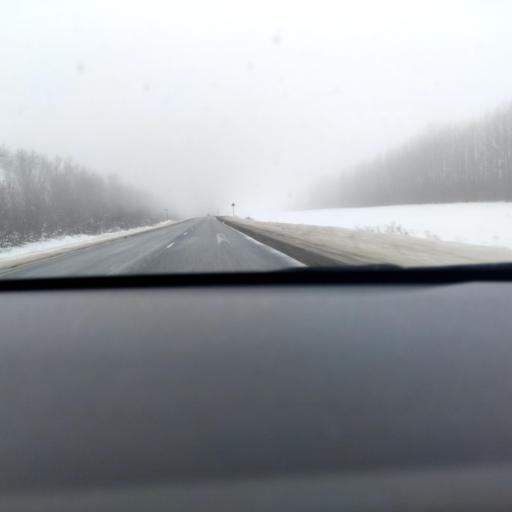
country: RU
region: Tatarstan
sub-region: Chistopol'skiy Rayon
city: Chistopol'
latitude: 55.3321
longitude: 50.4786
